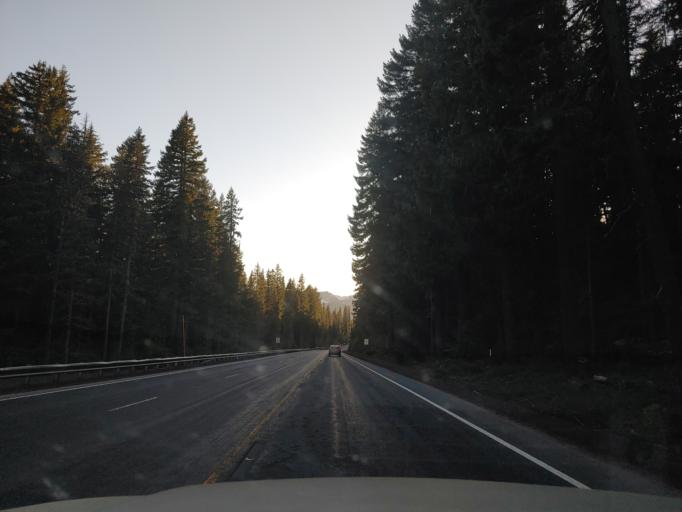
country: US
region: Oregon
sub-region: Lane County
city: Oakridge
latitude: 43.6190
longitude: -122.0766
